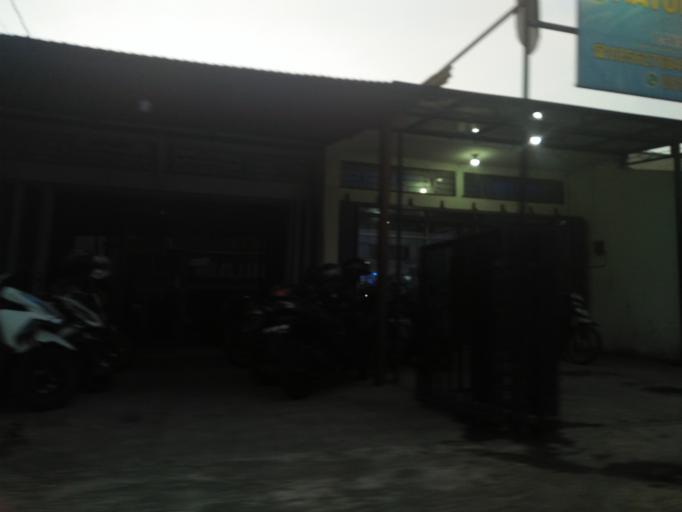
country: ID
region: Daerah Istimewa Yogyakarta
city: Sewon
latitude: -7.8411
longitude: 110.3915
